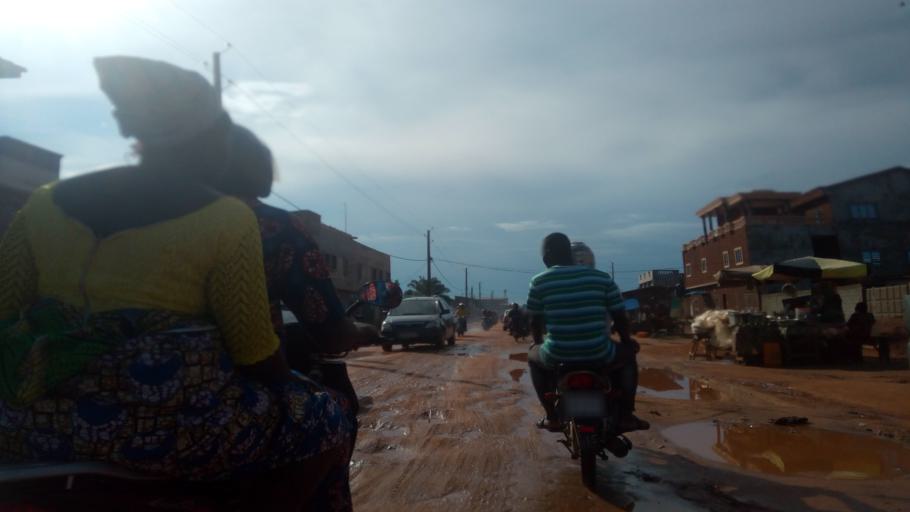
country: BJ
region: Atlantique
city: Abomey-Calavi
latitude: 6.4532
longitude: 2.3370
